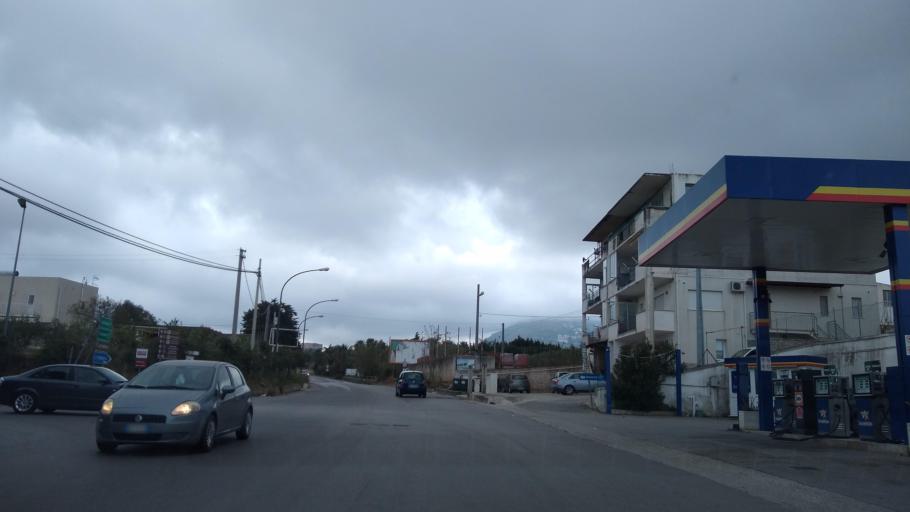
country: IT
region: Sicily
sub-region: Trapani
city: Alcamo
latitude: 37.9934
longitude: 12.9581
